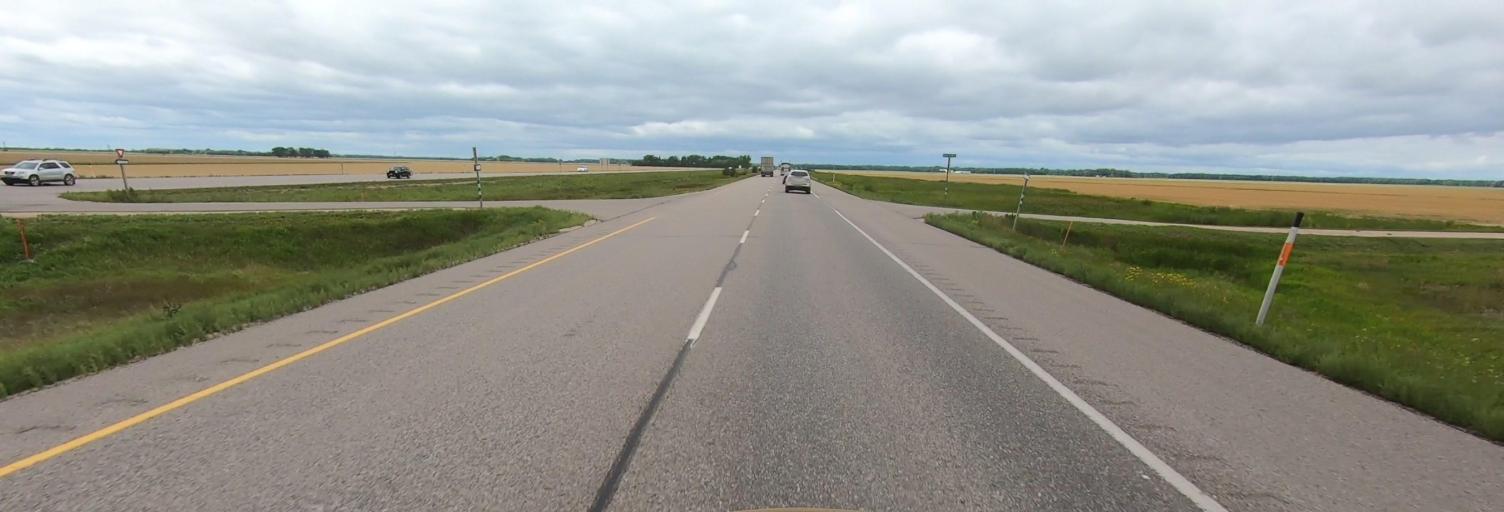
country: CA
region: Manitoba
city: Portage la Prairie
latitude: 49.9579
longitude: -98.0322
